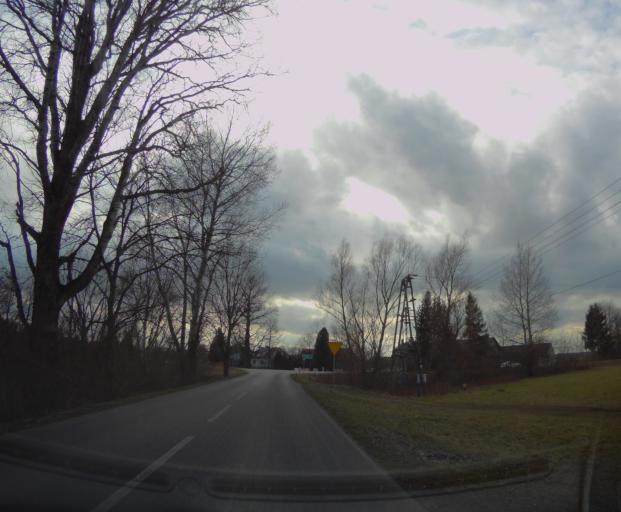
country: PL
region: Subcarpathian Voivodeship
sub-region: Powiat nizanski
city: Ulanow
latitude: 50.4744
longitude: 22.2498
